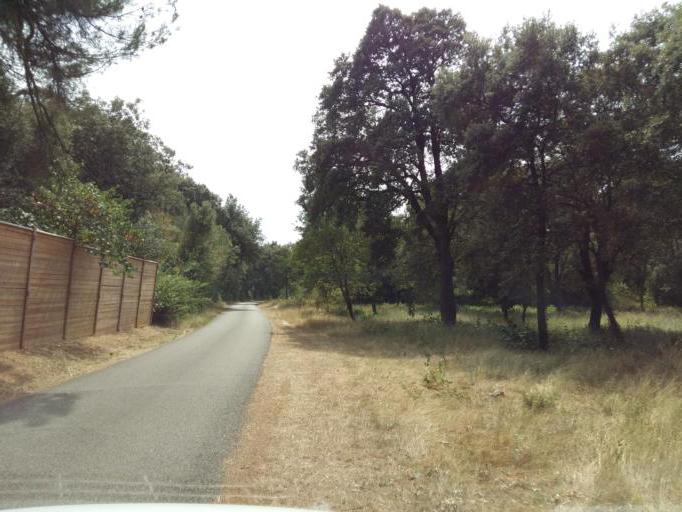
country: FR
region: Provence-Alpes-Cote d'Azur
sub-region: Departement du Vaucluse
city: Piolenc
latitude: 44.1718
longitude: 4.7857
